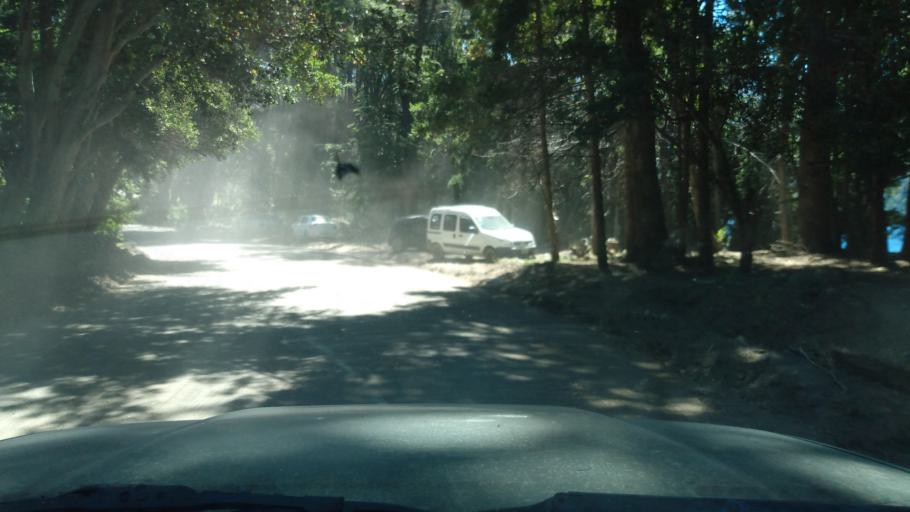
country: AR
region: Neuquen
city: Villa La Angostura
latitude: -40.6168
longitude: -71.5275
